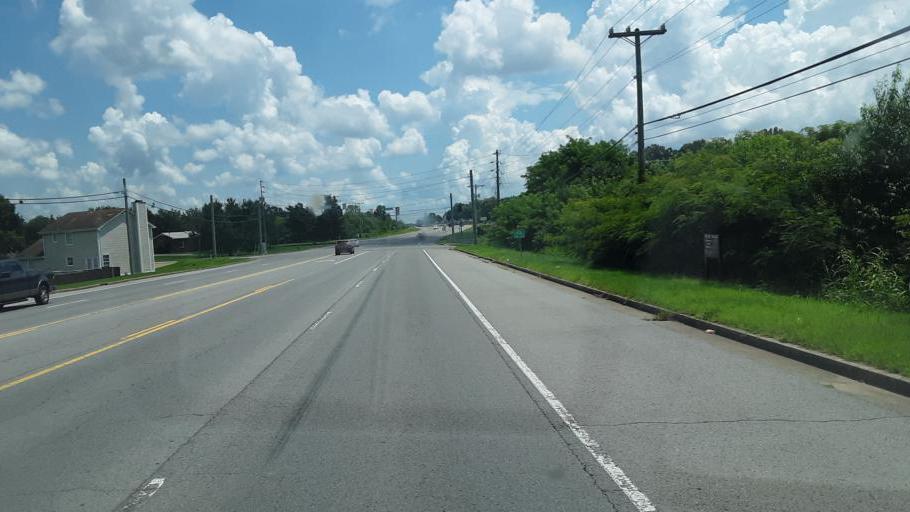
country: US
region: Kentucky
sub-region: Christian County
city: Oak Grove
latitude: 36.6320
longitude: -87.4092
